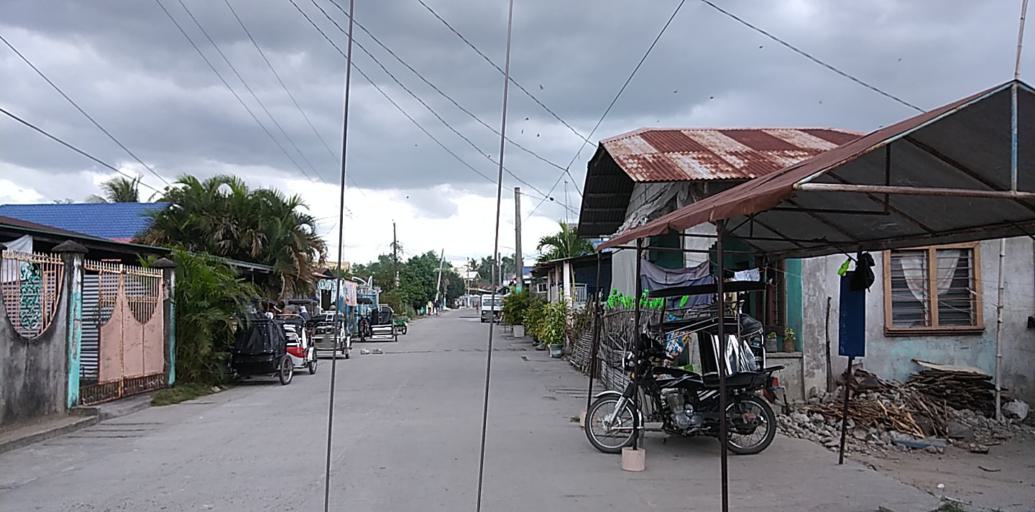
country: PH
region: Central Luzon
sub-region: Province of Pampanga
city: Pio
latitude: 15.0463
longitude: 120.5381
